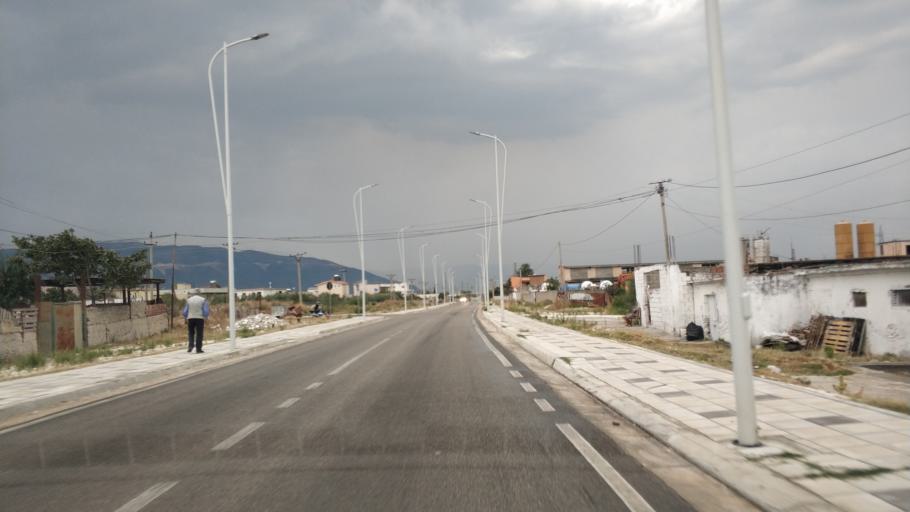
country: AL
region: Vlore
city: Vlore
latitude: 40.4790
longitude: 19.4670
